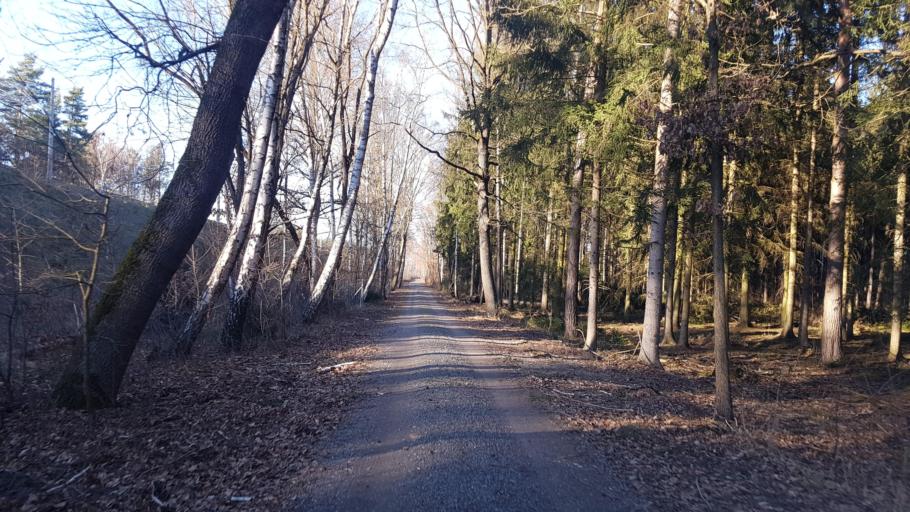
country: DE
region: Brandenburg
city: Hohenleipisch
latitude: 51.5056
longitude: 13.5769
